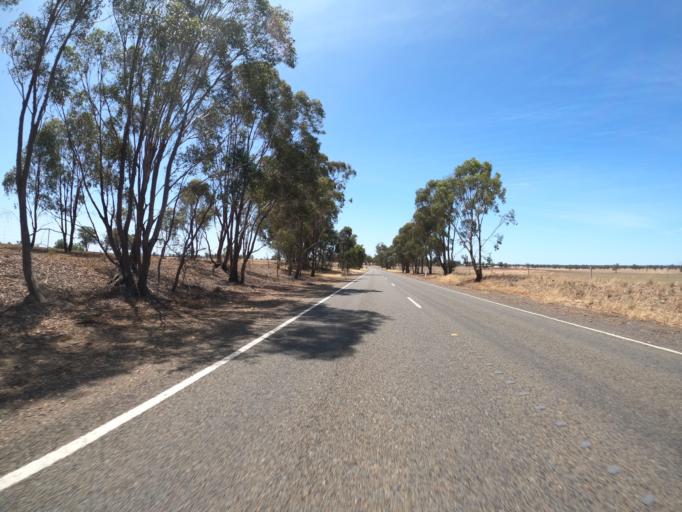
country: AU
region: Victoria
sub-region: Moira
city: Yarrawonga
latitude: -36.1016
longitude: 145.9927
